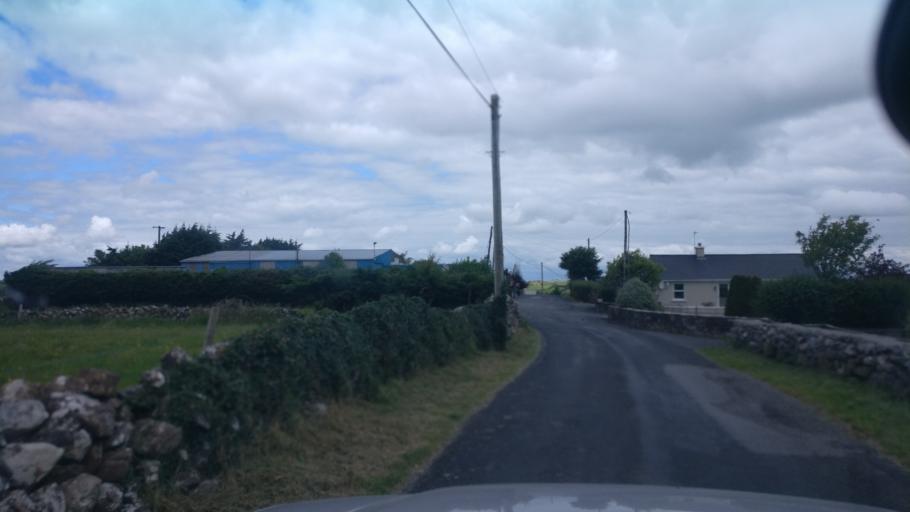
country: IE
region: Connaught
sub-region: County Galway
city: Loughrea
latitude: 53.1731
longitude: -8.5556
